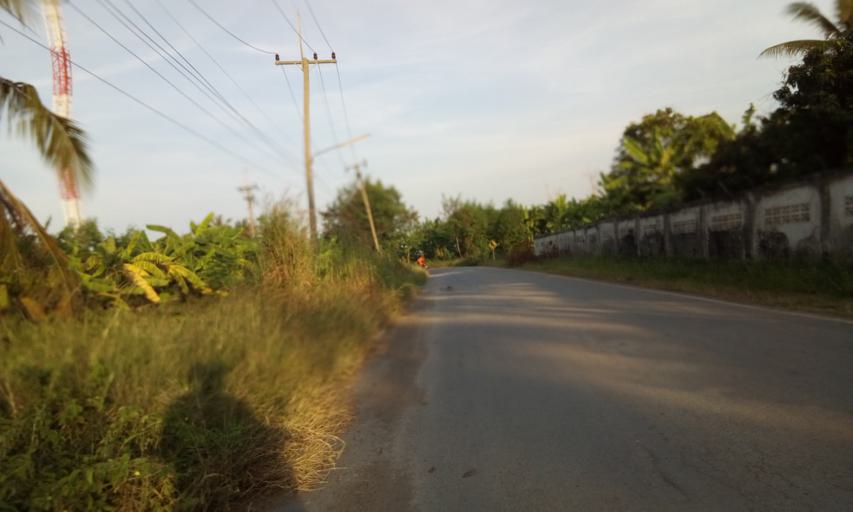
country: TH
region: Pathum Thani
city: Ban Lam Luk Ka
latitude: 14.0353
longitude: 100.8460
